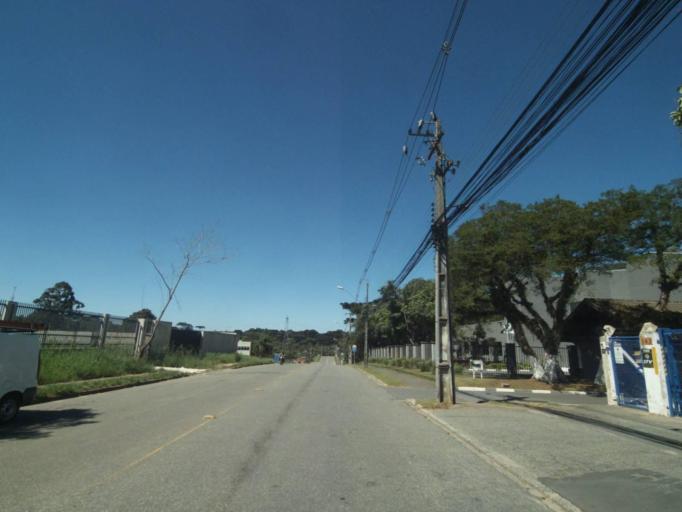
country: BR
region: Parana
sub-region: Curitiba
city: Curitiba
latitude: -25.4701
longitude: -49.3508
